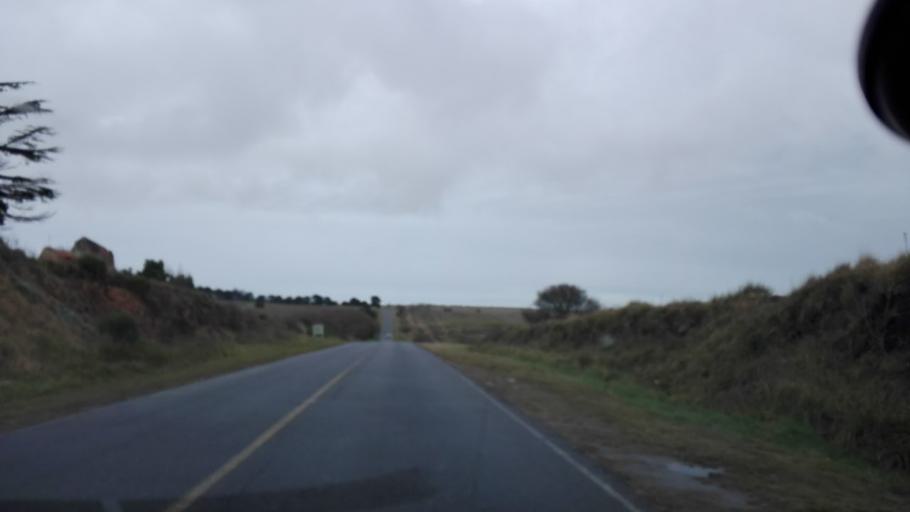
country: AR
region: Buenos Aires
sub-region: Partido de Tandil
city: Tandil
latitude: -37.3492
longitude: -59.1729
